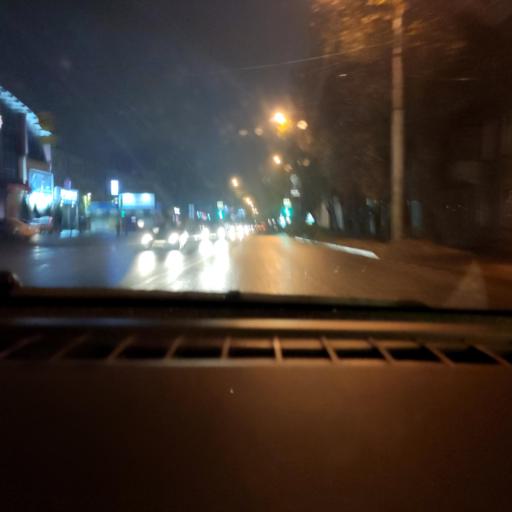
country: RU
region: Voronezj
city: Voronezh
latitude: 51.6712
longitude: 39.1775
